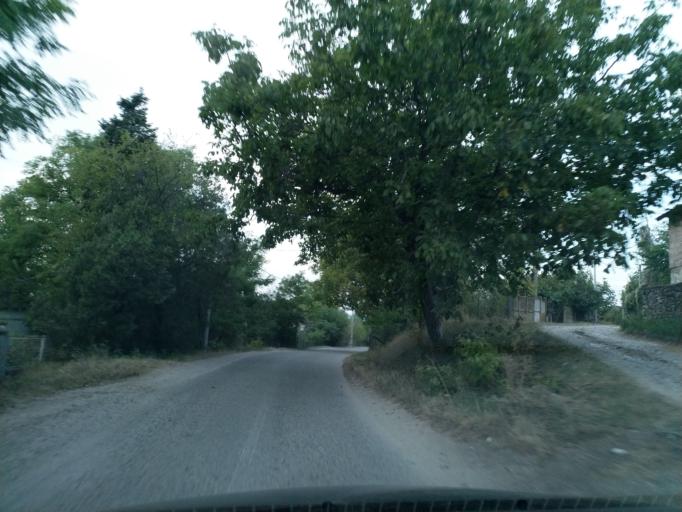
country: RS
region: Central Serbia
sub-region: Pomoravski Okrug
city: Paracin
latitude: 43.8490
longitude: 21.5280
